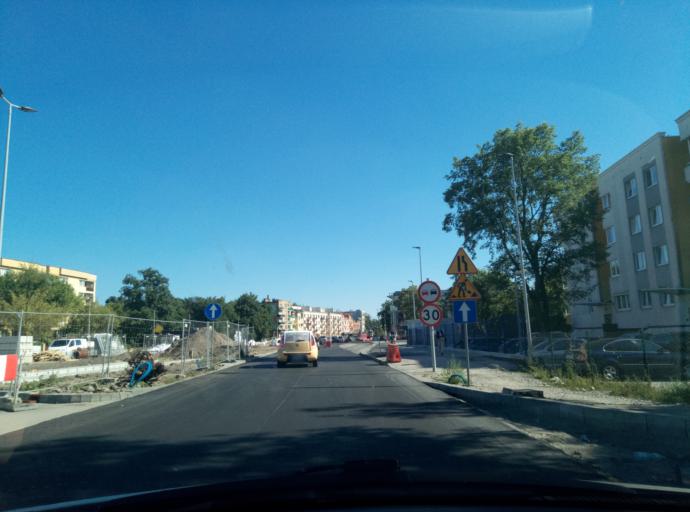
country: PL
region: Kujawsko-Pomorskie
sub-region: Torun
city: Torun
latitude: 53.0297
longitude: 18.5899
